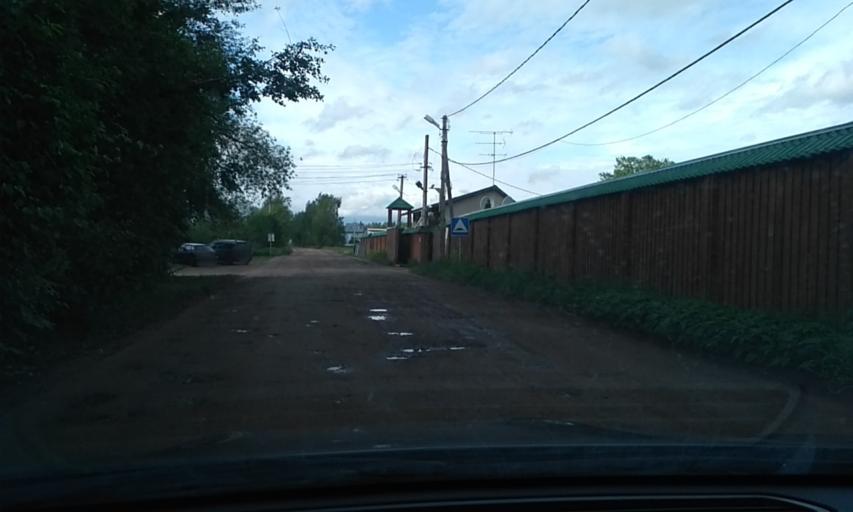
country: RU
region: Leningrad
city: Otradnoye
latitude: 59.7995
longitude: 30.8012
